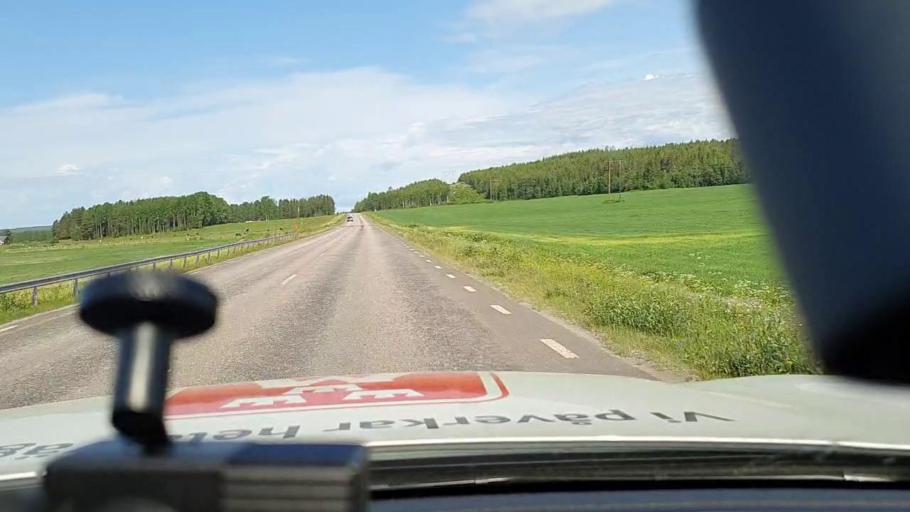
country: SE
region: Norrbotten
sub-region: Bodens Kommun
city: Boden
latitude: 65.9114
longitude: 21.3481
